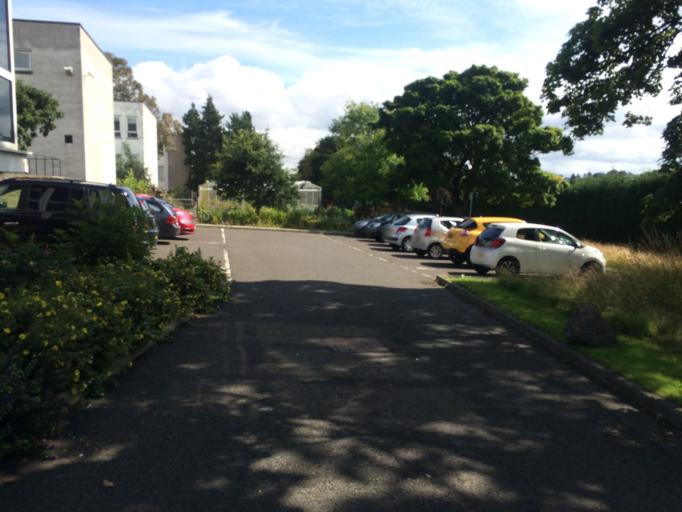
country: GB
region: Scotland
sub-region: Edinburgh
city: Edinburgh
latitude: 55.9213
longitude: -3.1777
